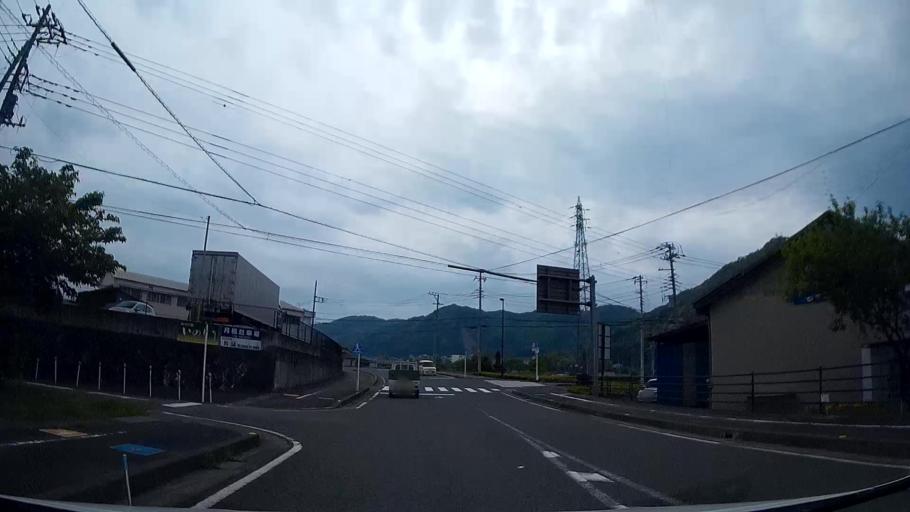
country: JP
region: Shizuoka
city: Ito
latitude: 34.9730
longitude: 138.9508
